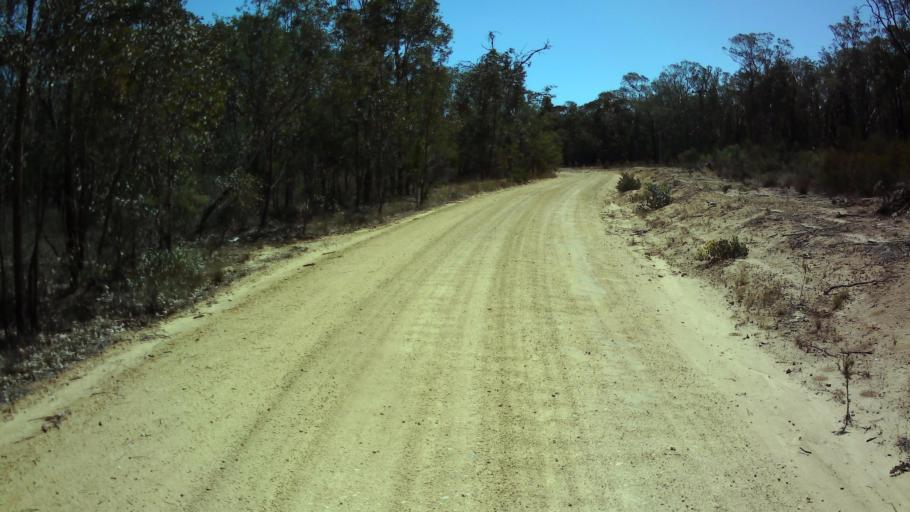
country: AU
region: New South Wales
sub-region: Cowra
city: Cowra
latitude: -33.8485
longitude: 148.4502
